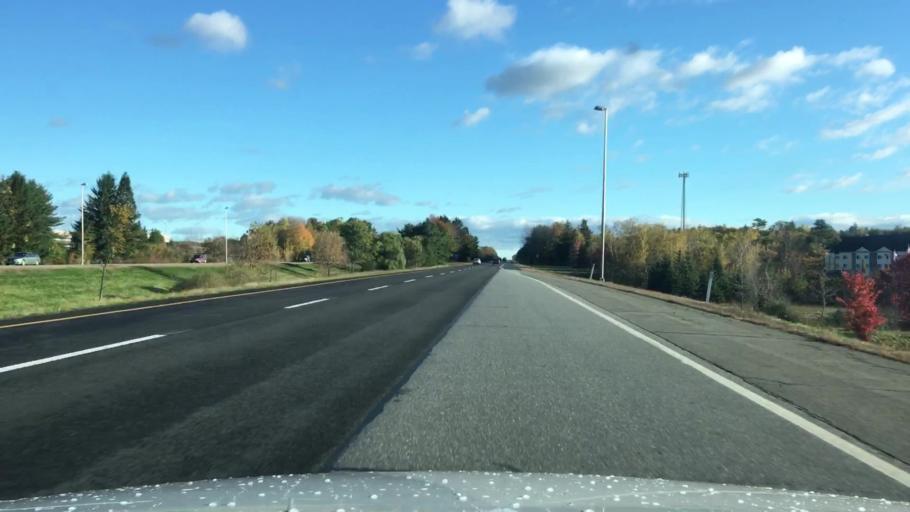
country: US
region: Maine
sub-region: Penobscot County
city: Veazie
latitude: 44.8343
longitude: -68.7396
